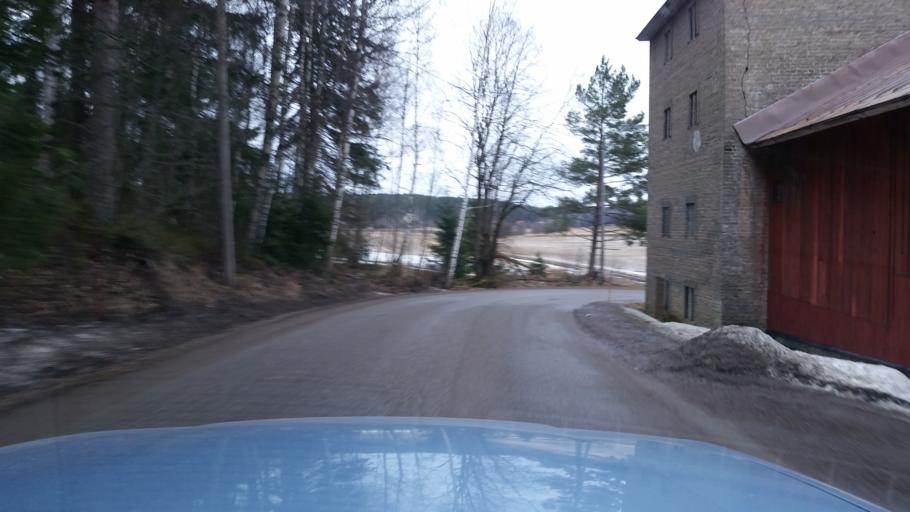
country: FI
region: Uusimaa
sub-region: Helsinki
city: Espoo
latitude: 60.2782
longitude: 24.6704
